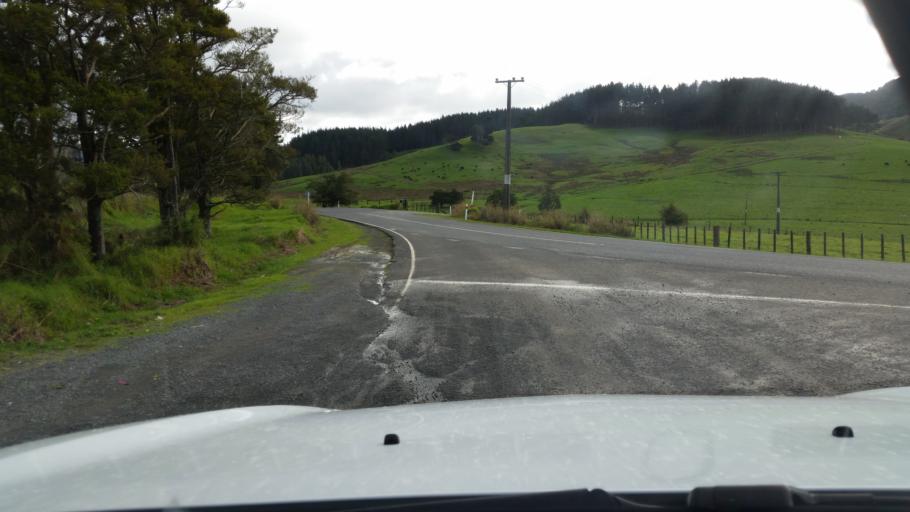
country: NZ
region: Northland
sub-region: Whangarei
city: Maungatapere
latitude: -35.6513
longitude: 174.1216
